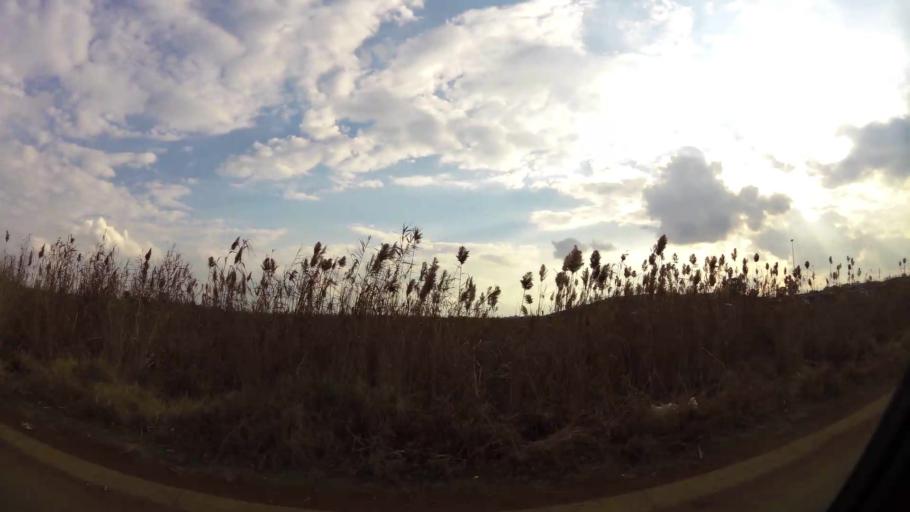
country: ZA
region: Gauteng
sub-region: Sedibeng District Municipality
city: Vanderbijlpark
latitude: -26.6705
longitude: 27.8678
